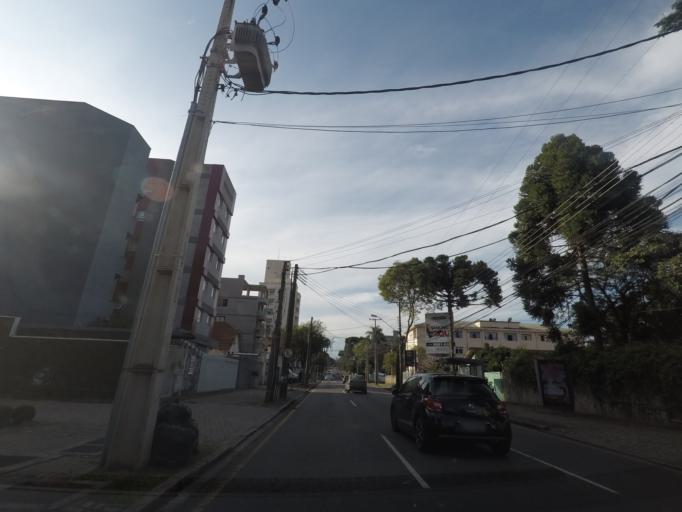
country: BR
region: Parana
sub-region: Curitiba
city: Curitiba
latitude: -25.4204
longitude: -49.2529
